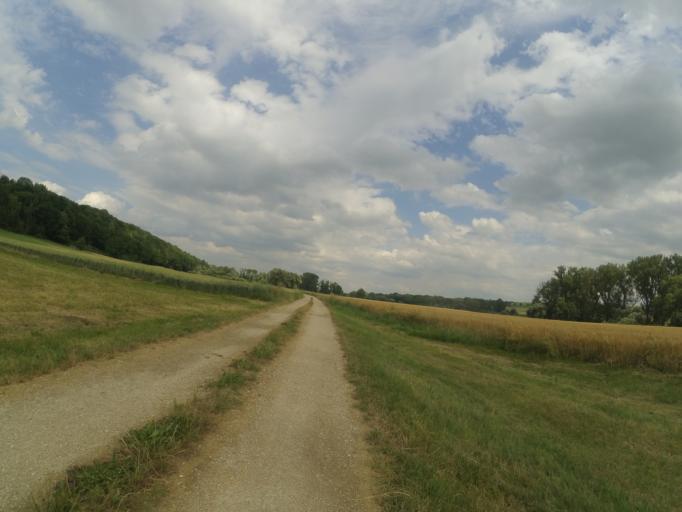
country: DE
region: Baden-Wuerttemberg
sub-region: Tuebingen Region
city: Ehingen
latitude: 48.2764
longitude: 9.7373
